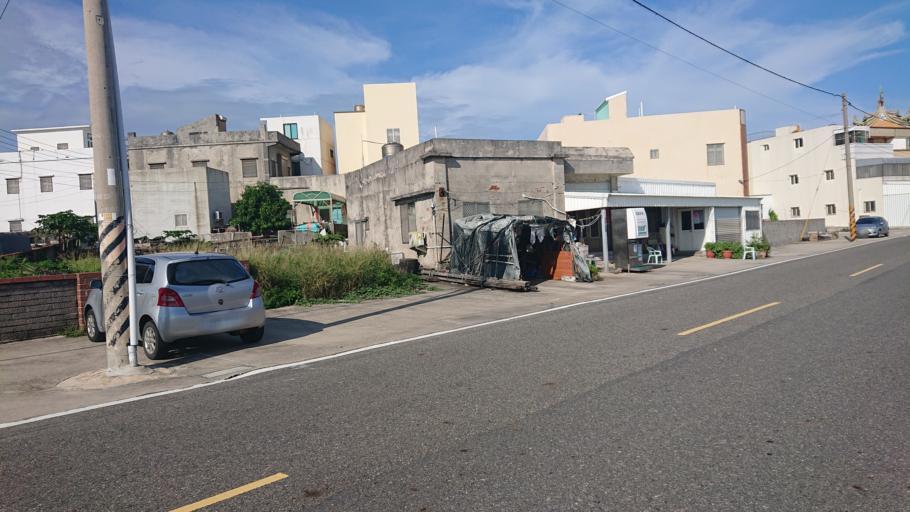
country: TW
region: Taiwan
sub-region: Penghu
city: Ma-kung
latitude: 23.5252
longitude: 119.5690
